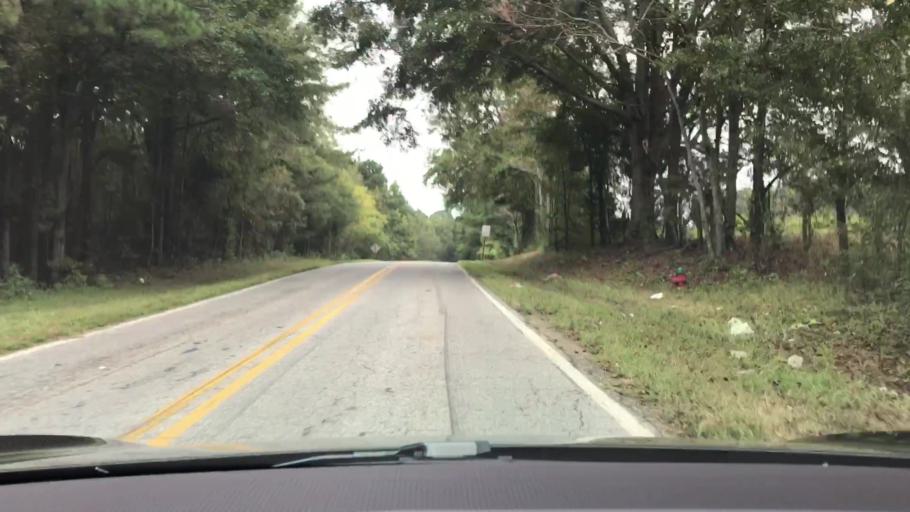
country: US
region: Georgia
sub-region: Barrow County
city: Auburn
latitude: 34.0327
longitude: -83.7963
